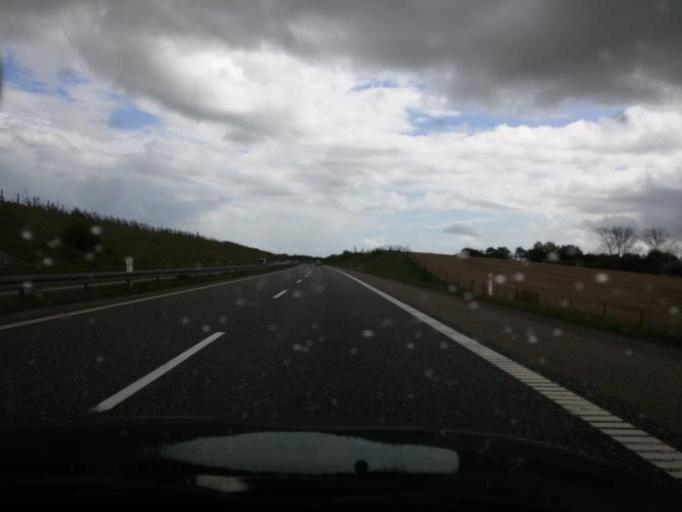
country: DK
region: South Denmark
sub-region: Faaborg-Midtfyn Kommune
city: Arslev
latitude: 55.2872
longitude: 10.4466
